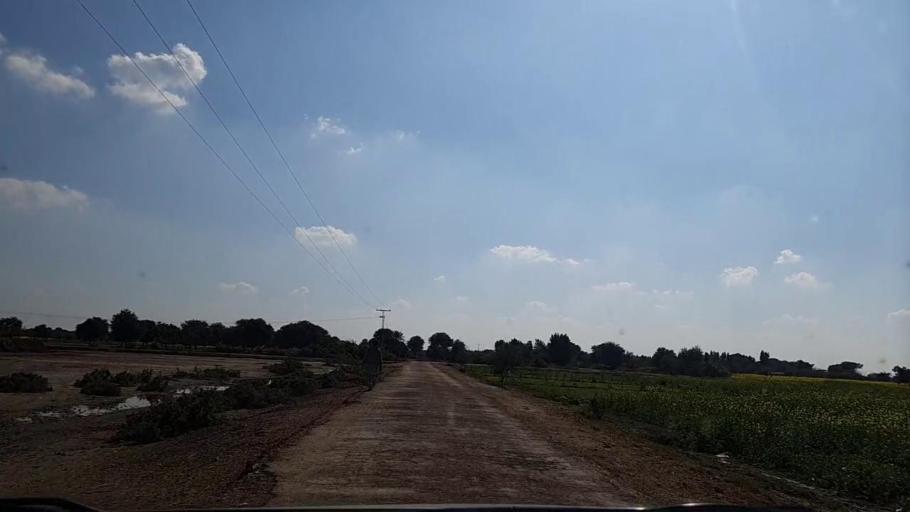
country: PK
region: Sindh
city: Pithoro
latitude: 25.6573
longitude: 69.4493
